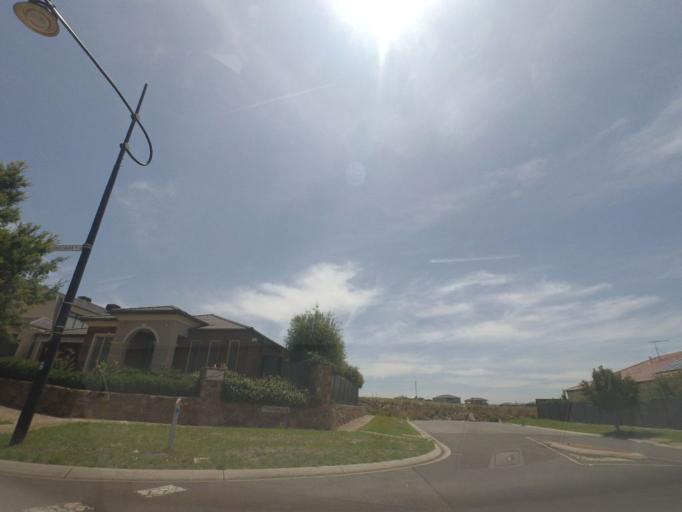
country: AU
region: Victoria
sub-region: Hume
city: Roxburgh Park
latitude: -37.6105
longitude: 144.9084
